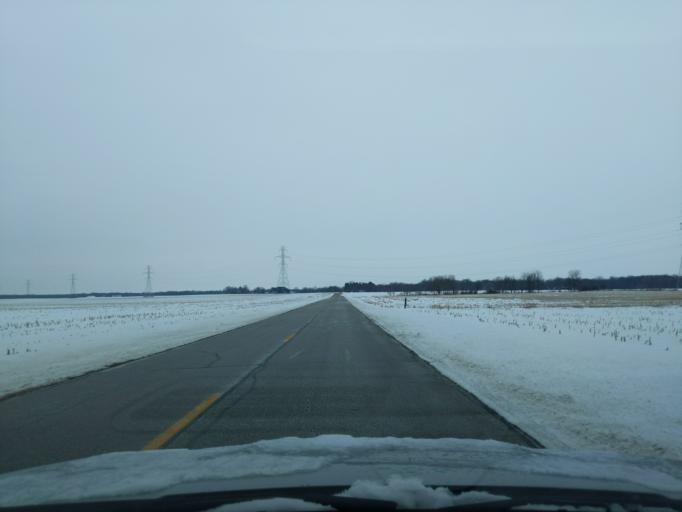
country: US
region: Indiana
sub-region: Benton County
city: Otterbein
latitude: 40.4169
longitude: -87.0845
